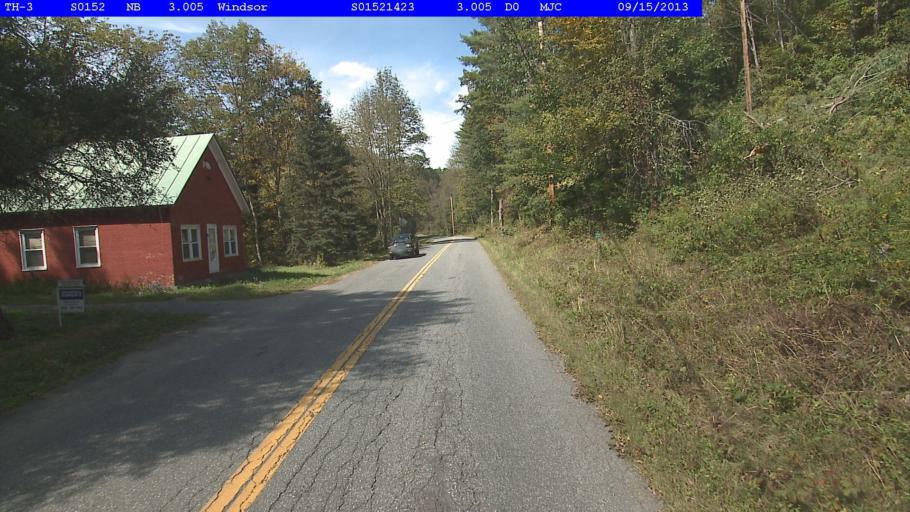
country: US
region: Vermont
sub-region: Windsor County
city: Windsor
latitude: 43.5060
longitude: -72.4278
